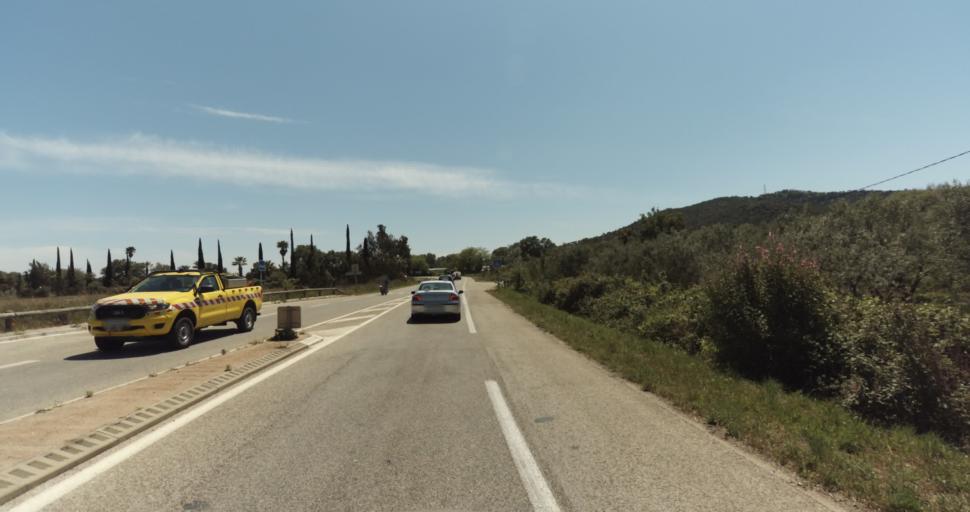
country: FR
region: Provence-Alpes-Cote d'Azur
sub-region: Departement du Var
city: Hyeres
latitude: 43.1437
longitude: 6.1537
